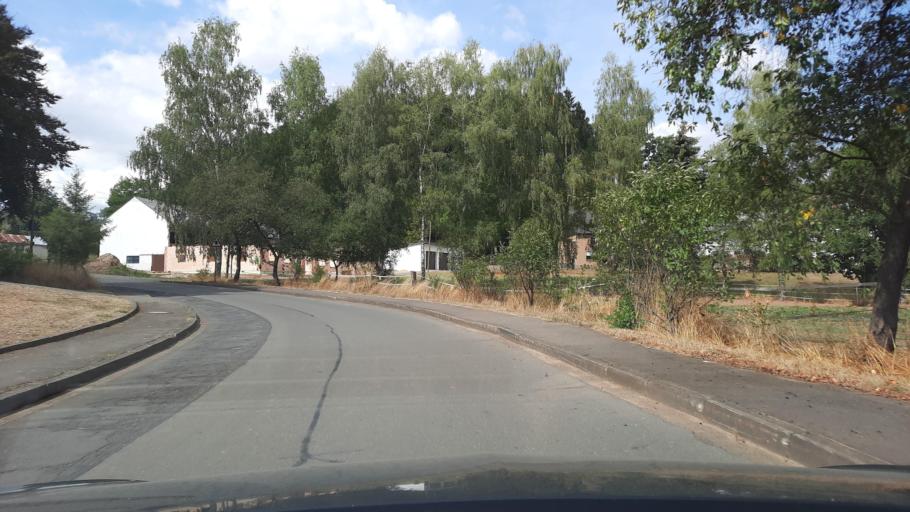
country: DE
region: Rheinland-Pfalz
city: Pittenbach
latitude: 50.1764
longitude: 6.3449
